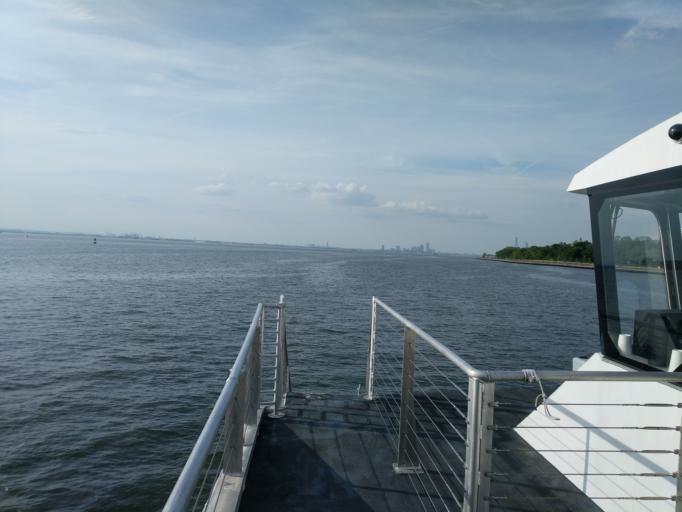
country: US
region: New York
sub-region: Kings County
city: Bensonhurst
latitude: 40.6183
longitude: -74.0438
